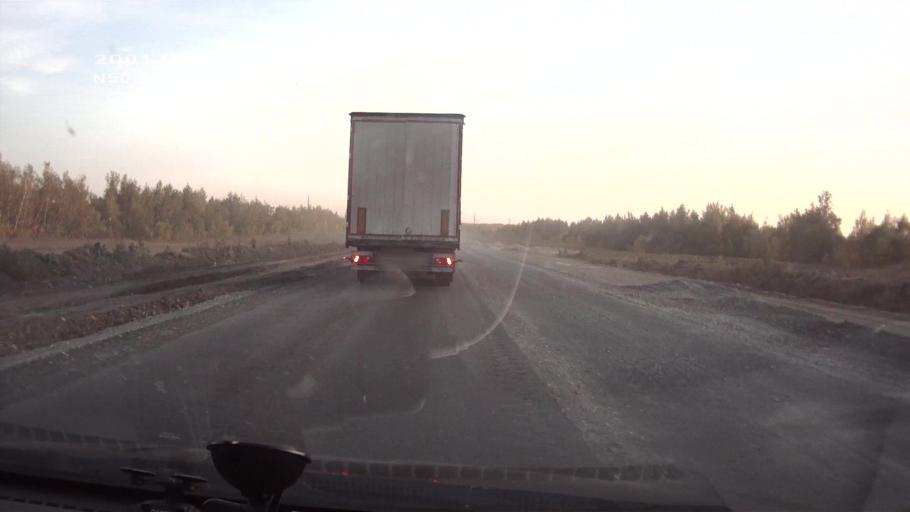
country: RU
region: Saratov
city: Kamenskiy
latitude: 50.9275
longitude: 45.5994
